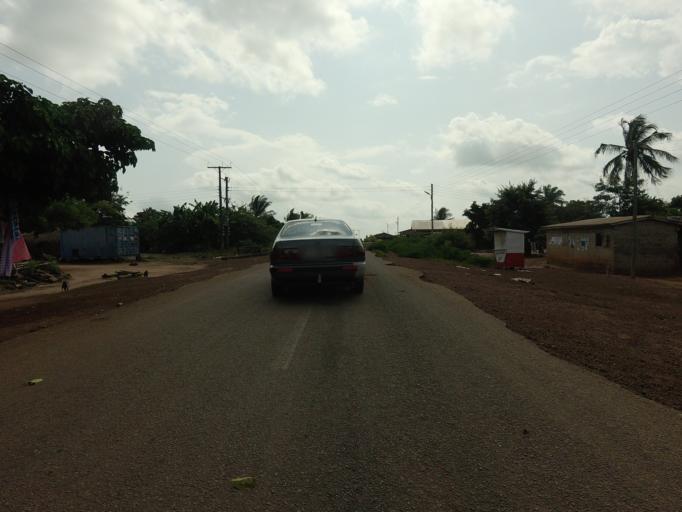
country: TG
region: Maritime
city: Lome
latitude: 6.2675
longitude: 0.9494
